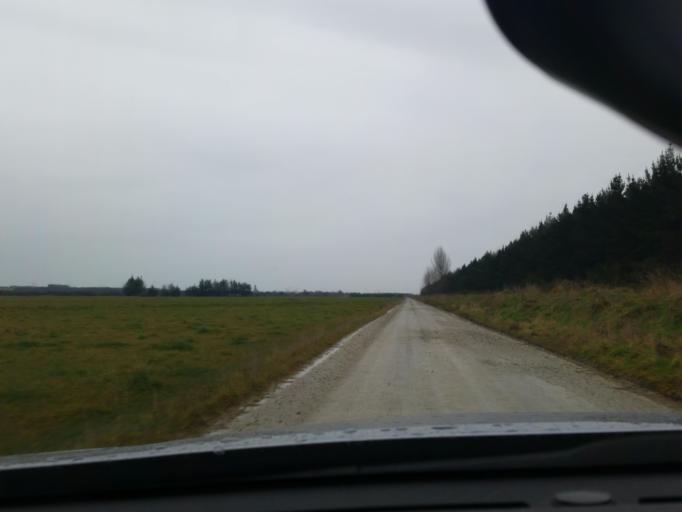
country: NZ
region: Southland
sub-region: Southland District
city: Winton
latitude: -46.2242
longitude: 168.4919
